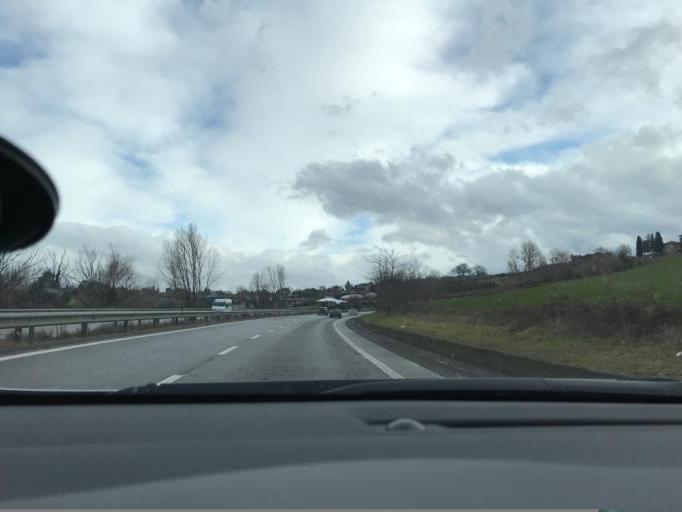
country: IT
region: Umbria
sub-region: Provincia di Perugia
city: Via Lippia
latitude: 43.1071
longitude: 12.4882
